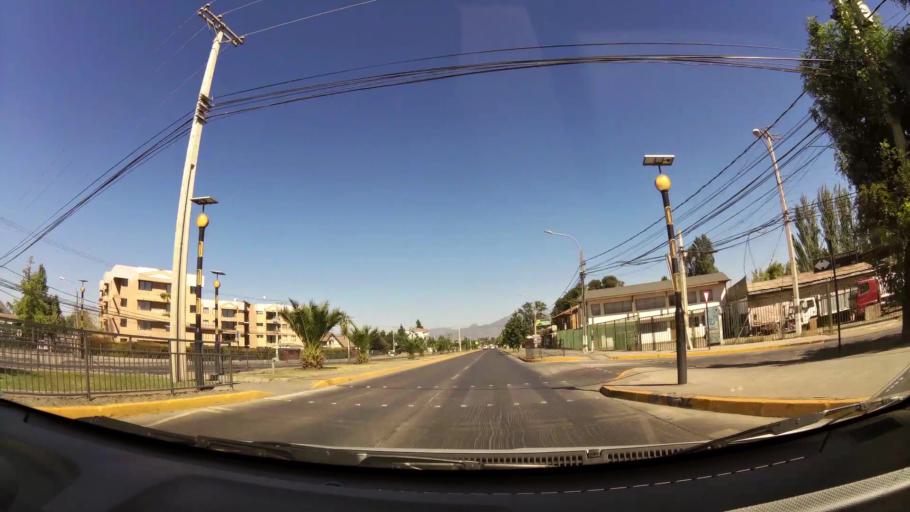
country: CL
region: O'Higgins
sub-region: Provincia de Cachapoal
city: Rancagua
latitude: -34.1751
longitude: -70.7065
